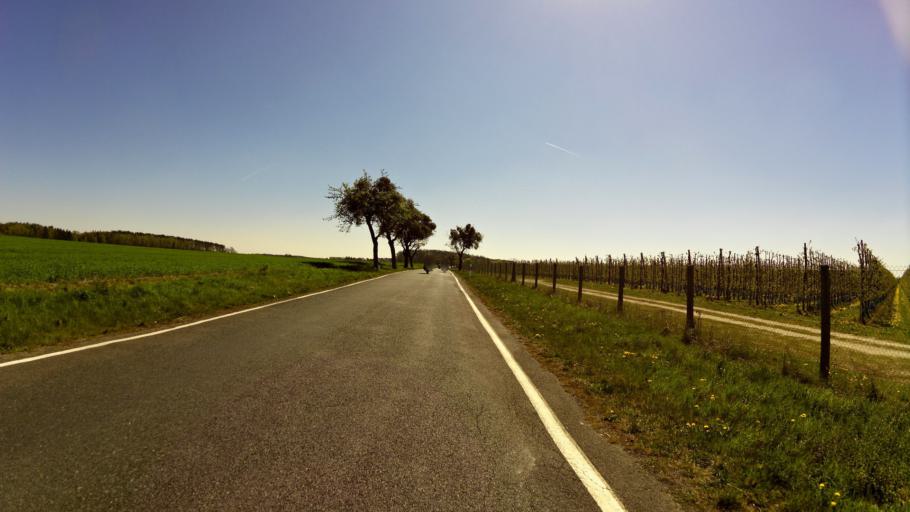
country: DE
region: Brandenburg
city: Werftpfuhl
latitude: 52.6324
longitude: 13.8088
